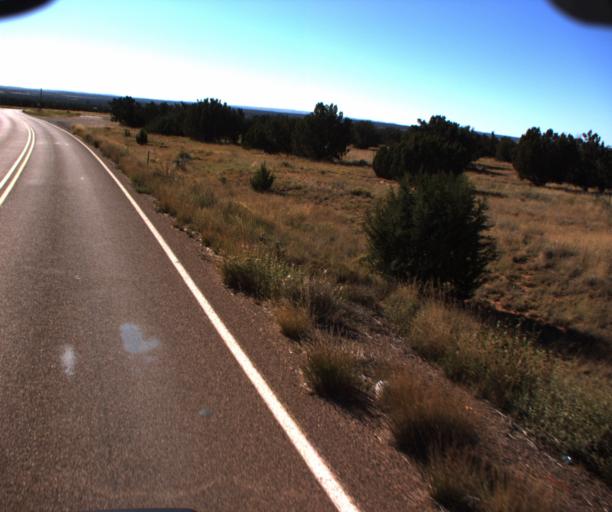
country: US
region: Arizona
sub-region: Navajo County
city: Heber-Overgaard
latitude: 34.4824
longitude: -110.3398
